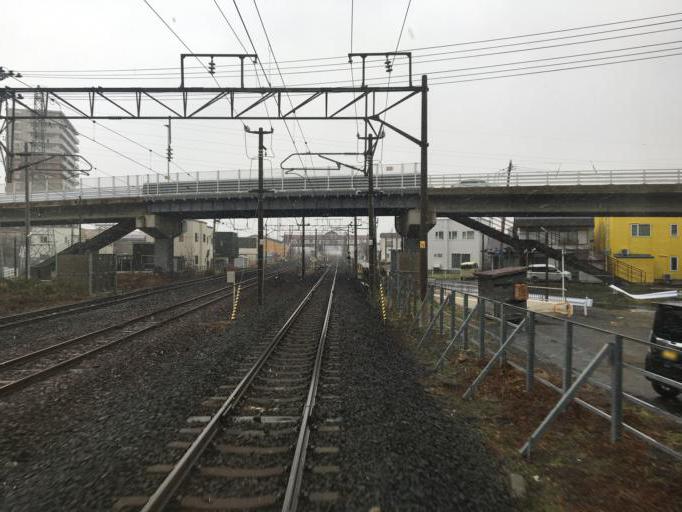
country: JP
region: Aomori
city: Aomori Shi
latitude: 40.8081
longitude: 140.7792
